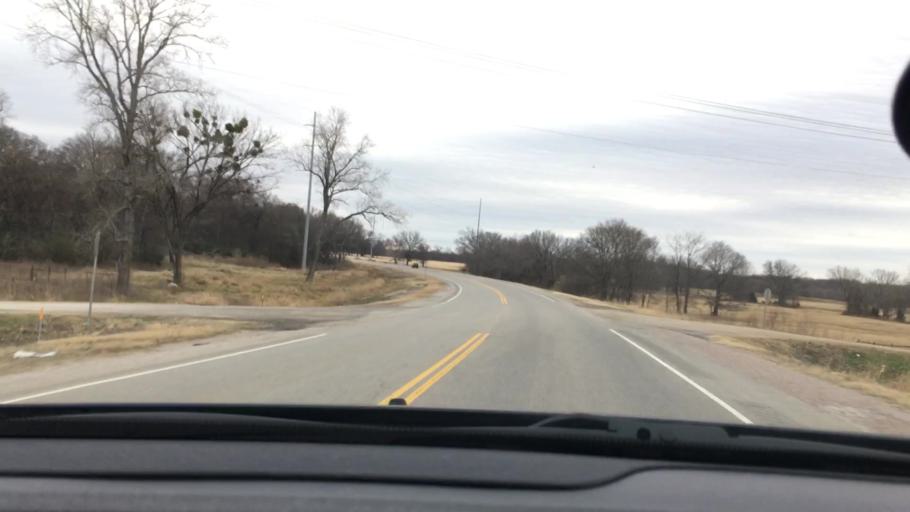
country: US
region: Oklahoma
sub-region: Marshall County
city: Oakland
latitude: 34.1898
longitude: -96.8035
